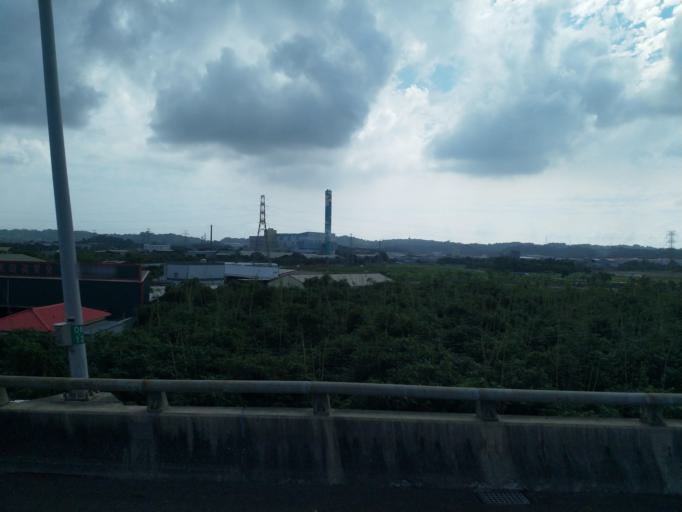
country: TW
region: Taiwan
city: Fengshan
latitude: 22.7007
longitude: 120.3594
